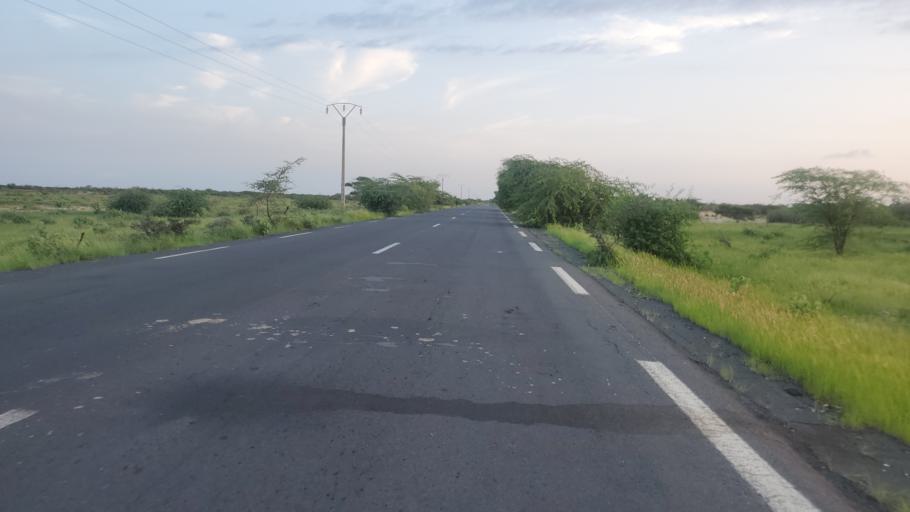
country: SN
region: Saint-Louis
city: Saint-Louis
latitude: 16.1307
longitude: -16.4125
